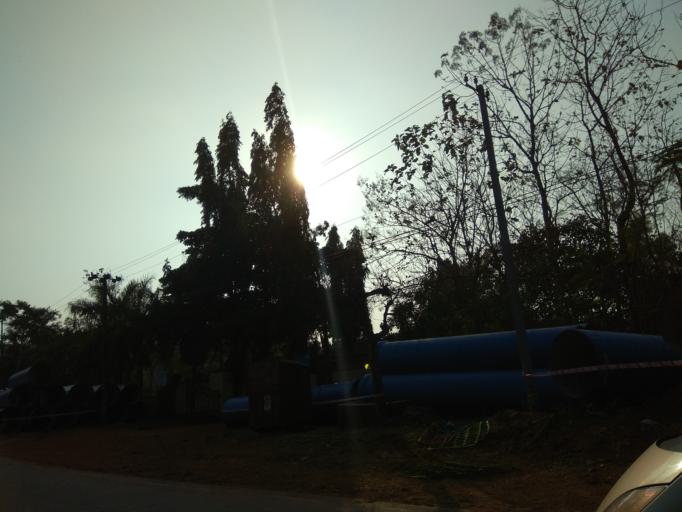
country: IN
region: Karnataka
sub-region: Dakshina Kannada
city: Mangalore
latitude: 12.9143
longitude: 74.8560
